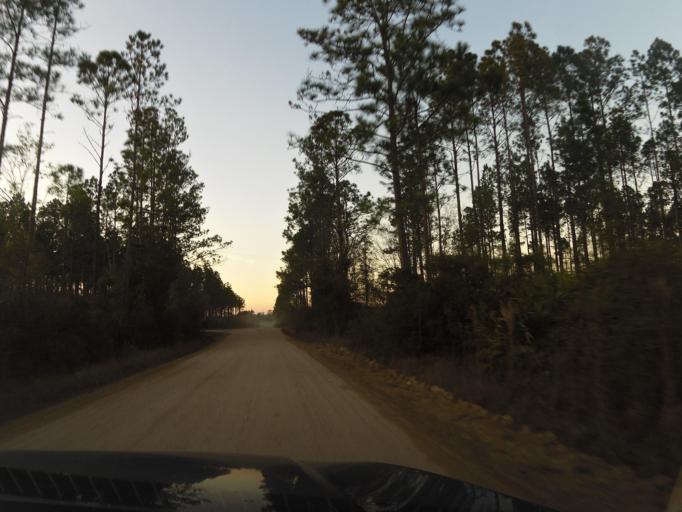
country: US
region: Florida
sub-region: Clay County
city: Asbury Lake
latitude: 29.9583
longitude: -81.7906
